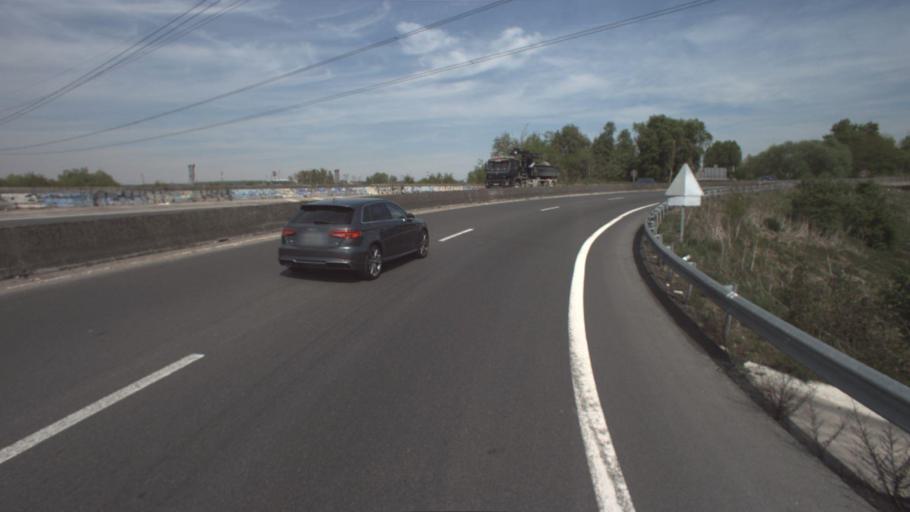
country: FR
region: Ile-de-France
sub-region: Departement de Seine-et-Marne
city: Saint-Thibault-des-Vignes
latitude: 48.8672
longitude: 2.6687
